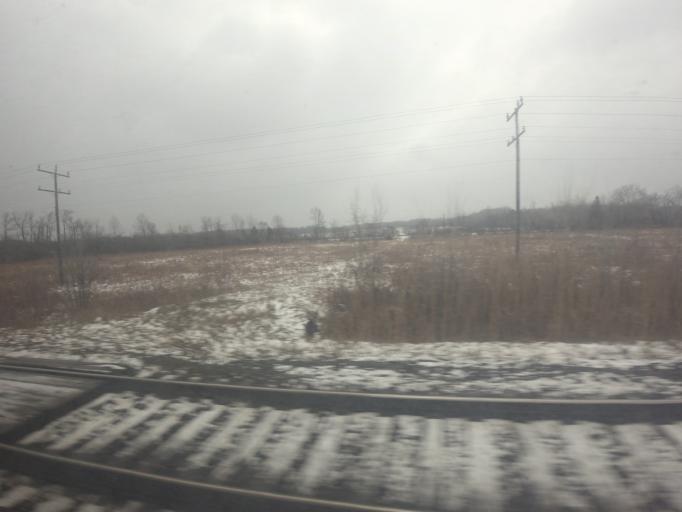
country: CA
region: Ontario
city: Quinte West
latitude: 44.0261
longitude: -77.7761
